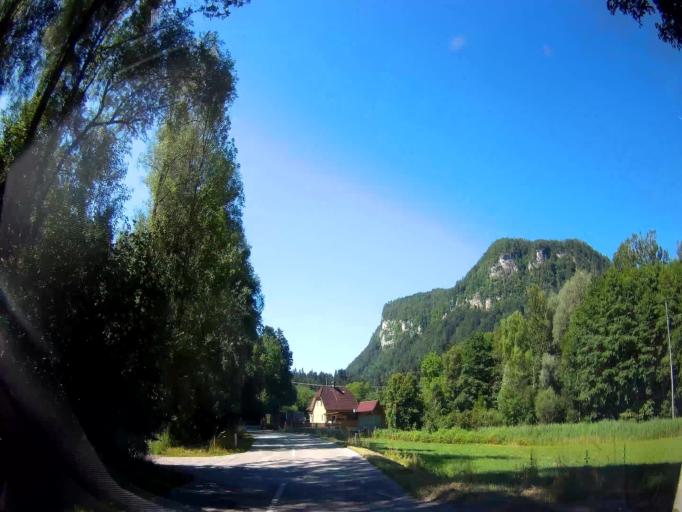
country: AT
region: Carinthia
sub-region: Politischer Bezirk Klagenfurt Land
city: Grafenstein
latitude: 46.6009
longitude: 14.4395
